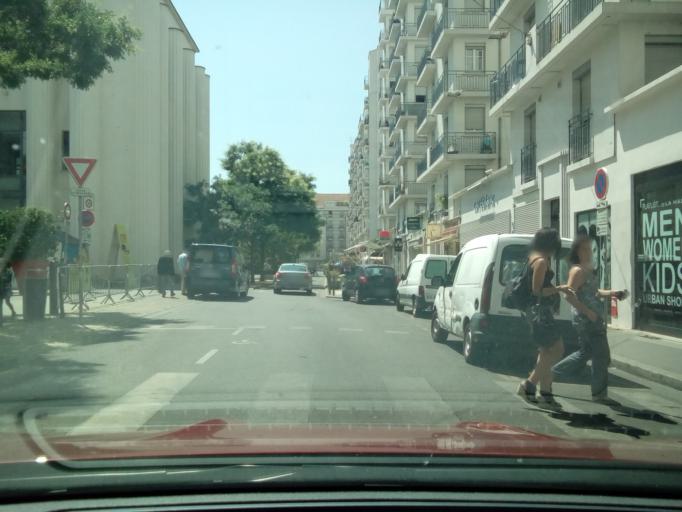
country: FR
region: Rhone-Alpes
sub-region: Departement du Rhone
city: Villeurbanne
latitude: 45.7669
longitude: 4.8789
